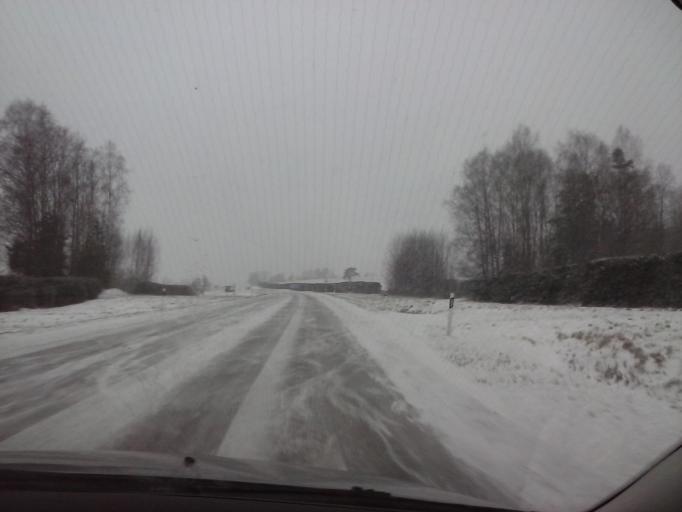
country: EE
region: Valgamaa
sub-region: Torva linn
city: Torva
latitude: 58.0423
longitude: 26.1884
